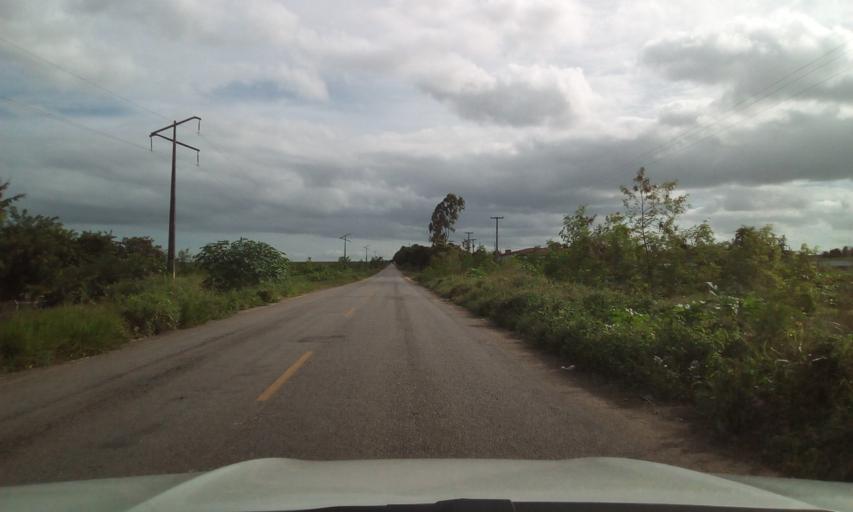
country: BR
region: Paraiba
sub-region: Santa Rita
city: Santa Rita
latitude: -6.9730
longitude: -34.9754
